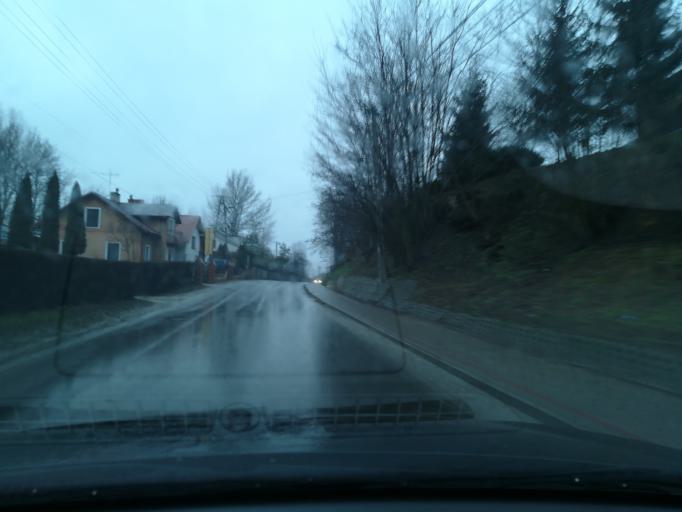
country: PL
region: Subcarpathian Voivodeship
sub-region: Powiat lancucki
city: Kosina
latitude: 50.0734
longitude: 22.3290
